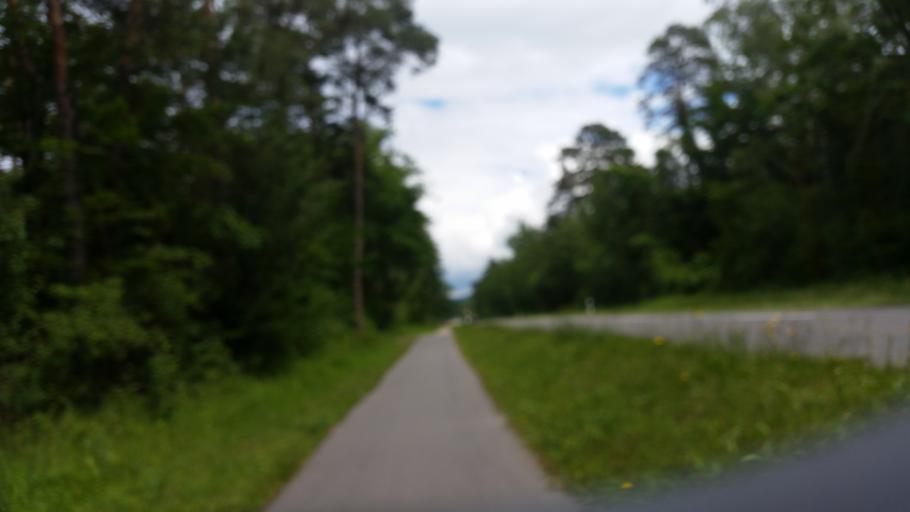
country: CH
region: Vaud
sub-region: Jura-Nord vaudois District
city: Yvonand
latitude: 46.7990
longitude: 6.7039
